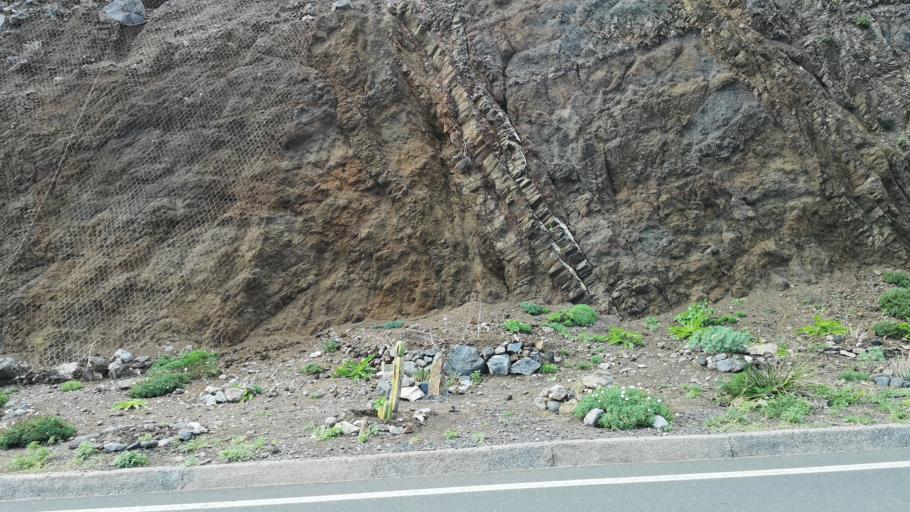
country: ES
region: Canary Islands
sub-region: Provincia de Santa Cruz de Tenerife
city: Agulo
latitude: 28.1809
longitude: -17.1865
